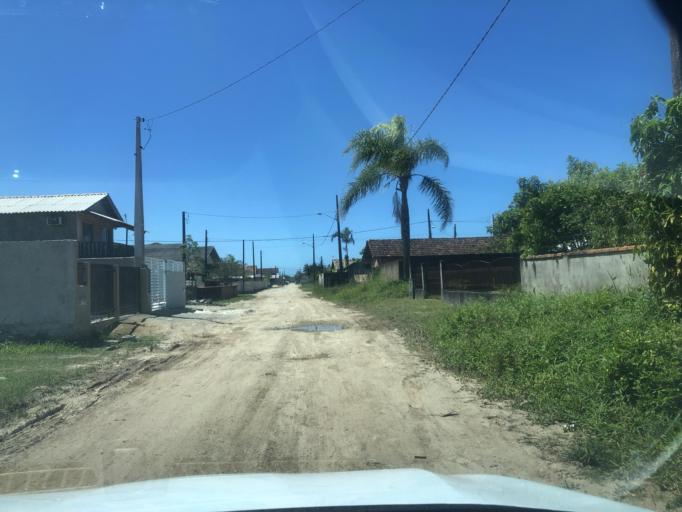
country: BR
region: Santa Catarina
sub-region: Sao Francisco Do Sul
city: Sao Francisco do Sul
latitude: -26.2320
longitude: -48.5209
